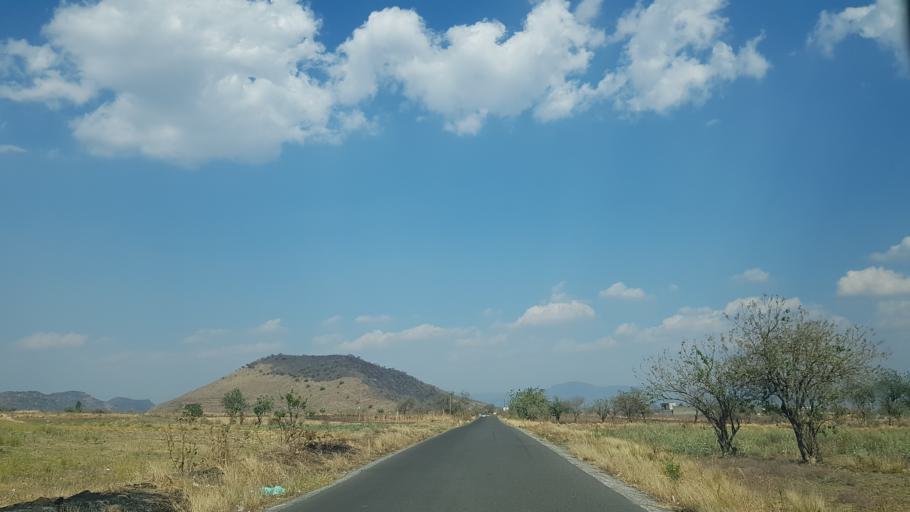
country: MX
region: Puebla
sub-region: Tianguismanalco
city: San Martin Tlapala
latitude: 18.9236
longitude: -98.4905
